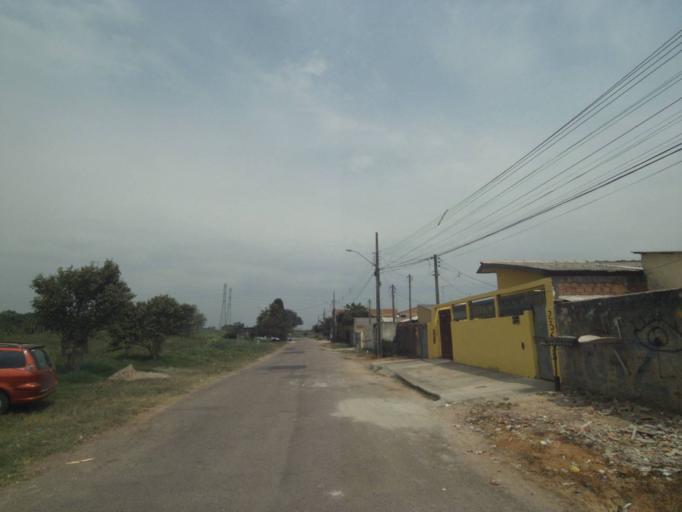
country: BR
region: Parana
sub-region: Pinhais
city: Pinhais
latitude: -25.4850
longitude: -49.1929
